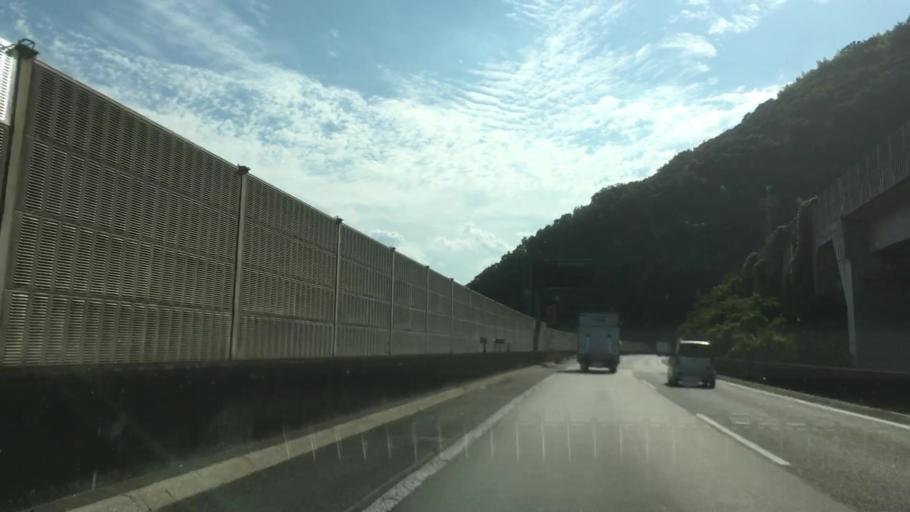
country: JP
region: Yamaguchi
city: Otake
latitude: 34.2204
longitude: 132.1993
